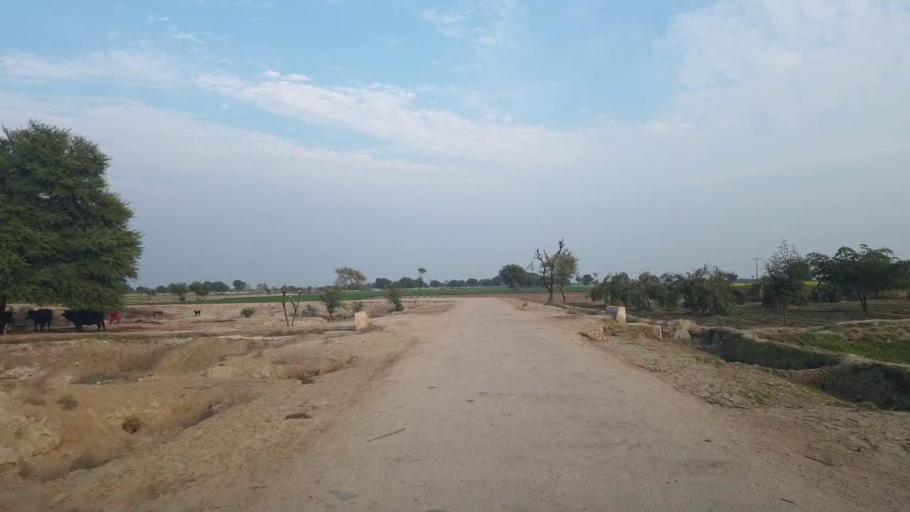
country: PK
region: Sindh
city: Shahpur Chakar
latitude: 26.0973
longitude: 68.5406
